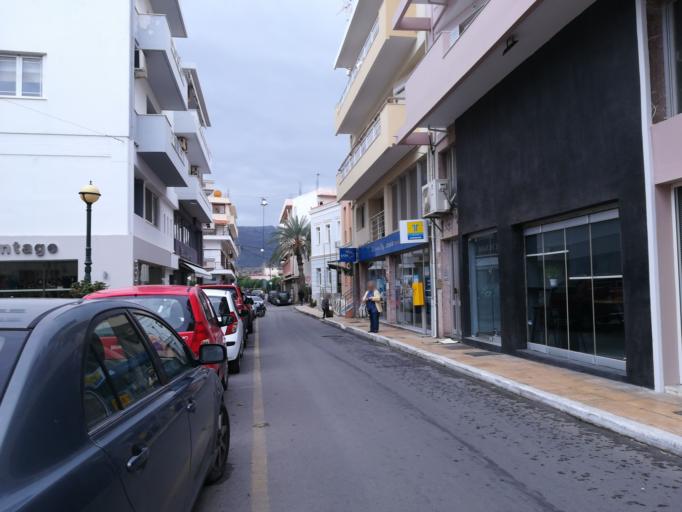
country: GR
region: Crete
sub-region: Nomos Lasithiou
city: Siteia
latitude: 35.2072
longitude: 26.1061
